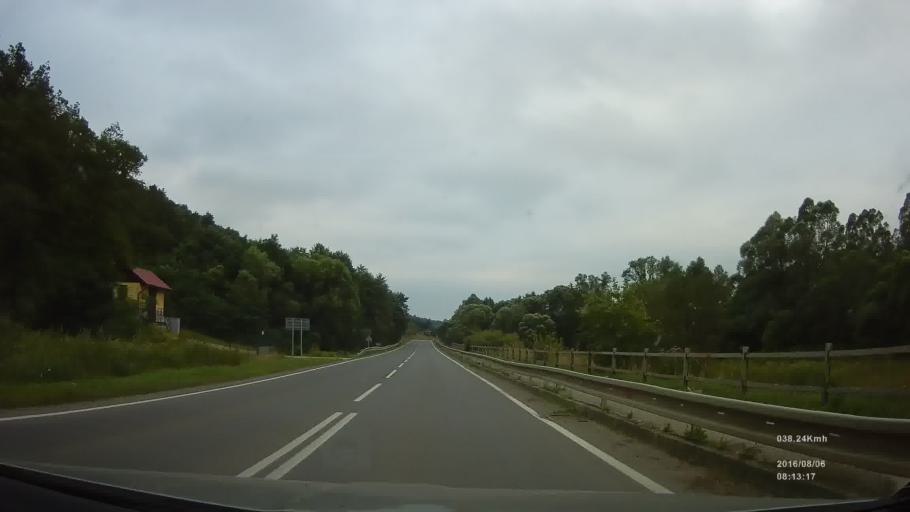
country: SK
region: Presovsky
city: Stropkov
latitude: 49.2250
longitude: 21.6638
